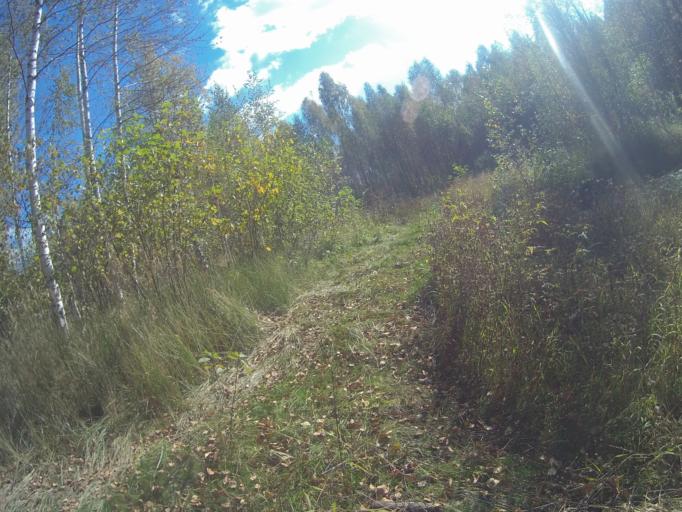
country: RU
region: Vladimir
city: Raduzhnyy
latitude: 55.9321
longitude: 40.1991
